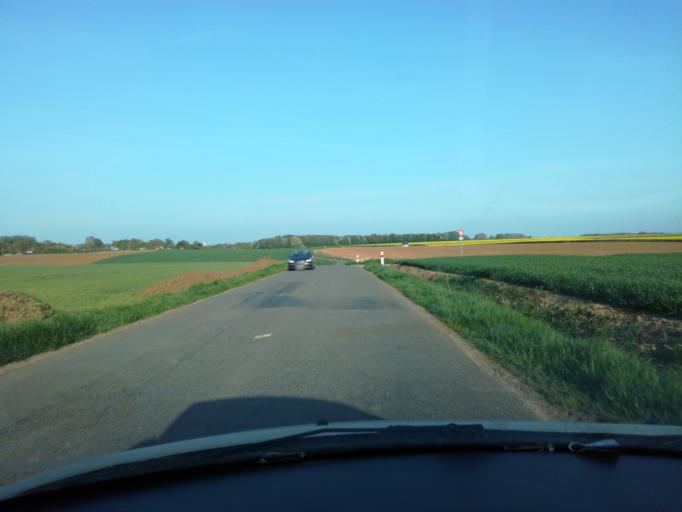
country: FR
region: Picardie
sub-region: Departement de la Somme
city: Poix-de-Picardie
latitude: 49.8167
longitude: 1.9847
